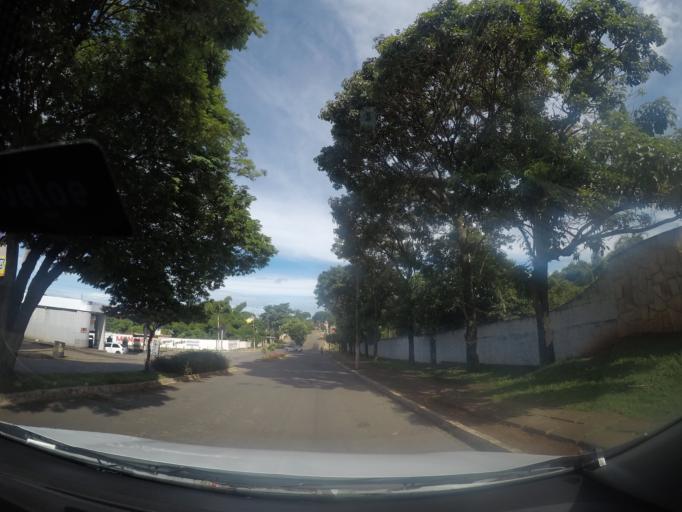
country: BR
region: Goias
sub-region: Inhumas
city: Inhumas
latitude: -16.3656
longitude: -49.4992
